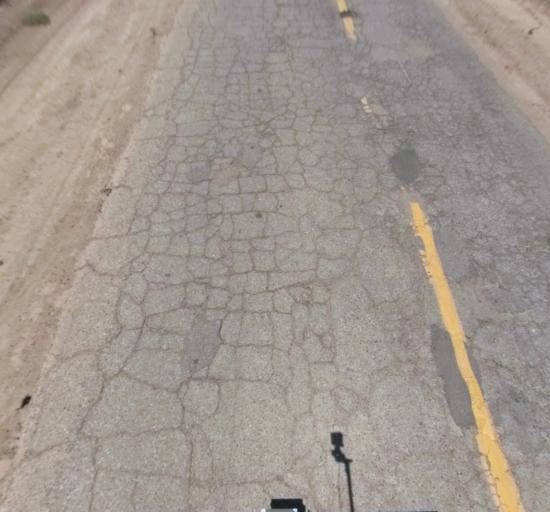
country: US
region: California
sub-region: Madera County
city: Fairmead
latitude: 36.9964
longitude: -120.1902
